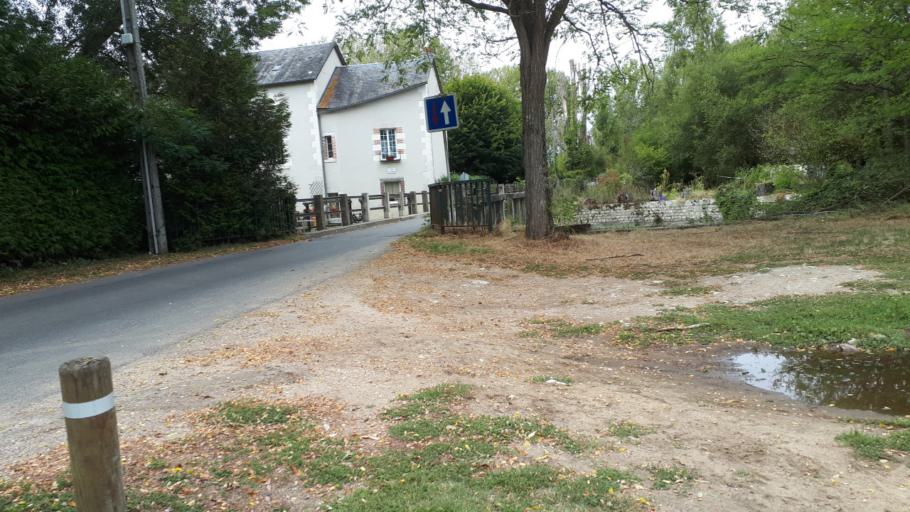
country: FR
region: Centre
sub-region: Departement du Loir-et-Cher
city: Saint-Gervais-la-Foret
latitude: 47.5681
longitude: 1.3428
